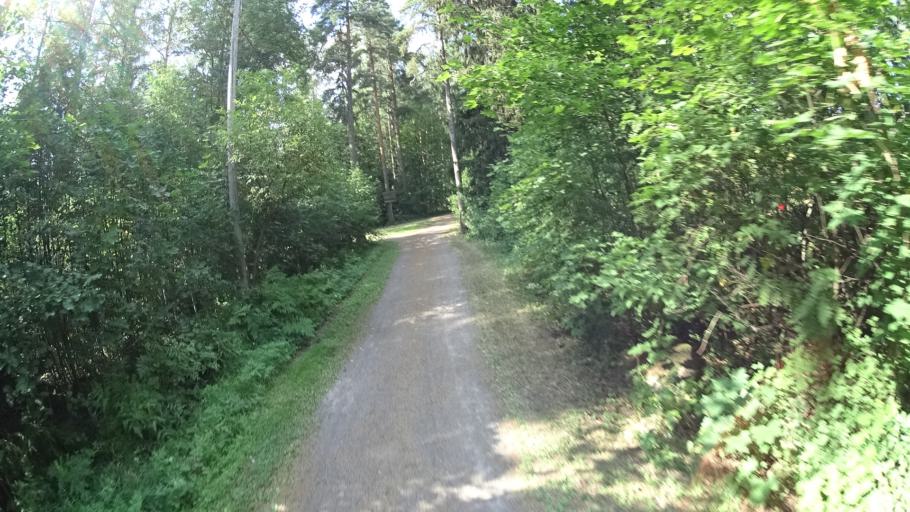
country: FI
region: Uusimaa
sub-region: Porvoo
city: Porvoo
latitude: 60.3809
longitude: 25.6929
